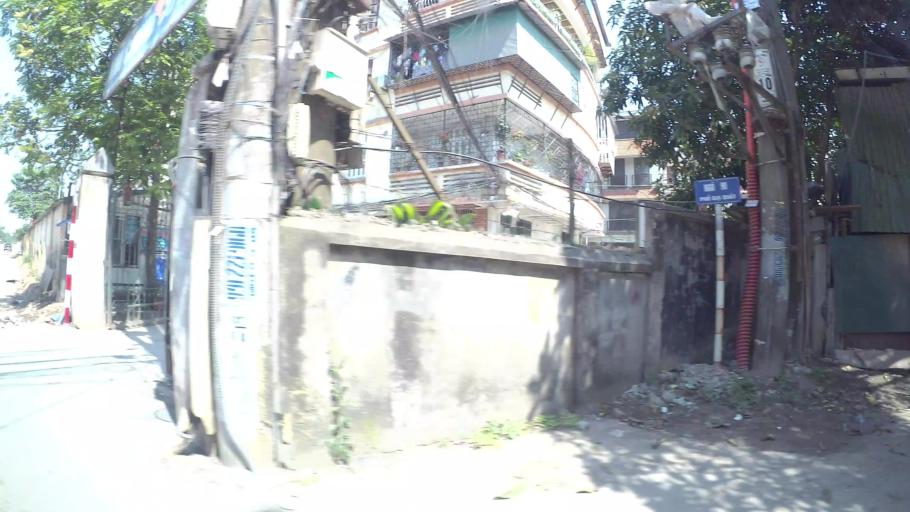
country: VN
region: Ha Noi
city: Hoan Kiem
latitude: 21.0565
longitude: 105.8772
